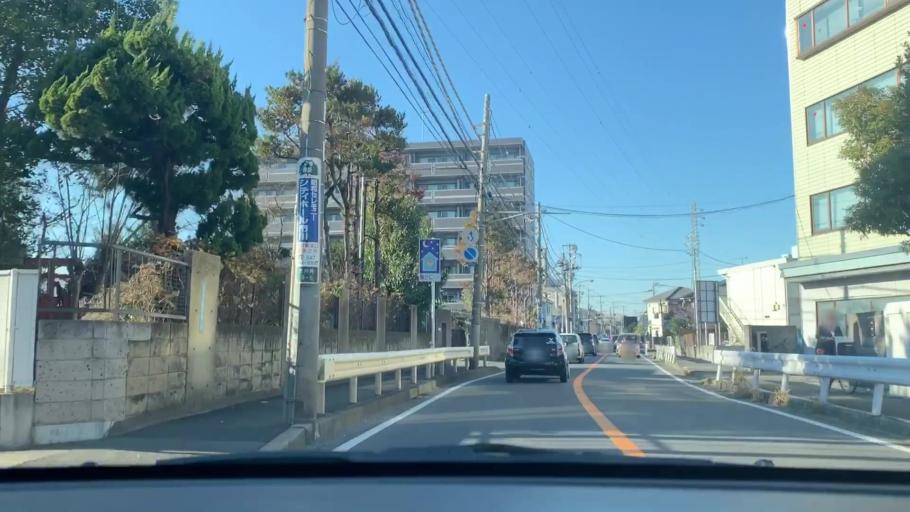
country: JP
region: Tokyo
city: Urayasu
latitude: 35.7237
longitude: 139.9038
